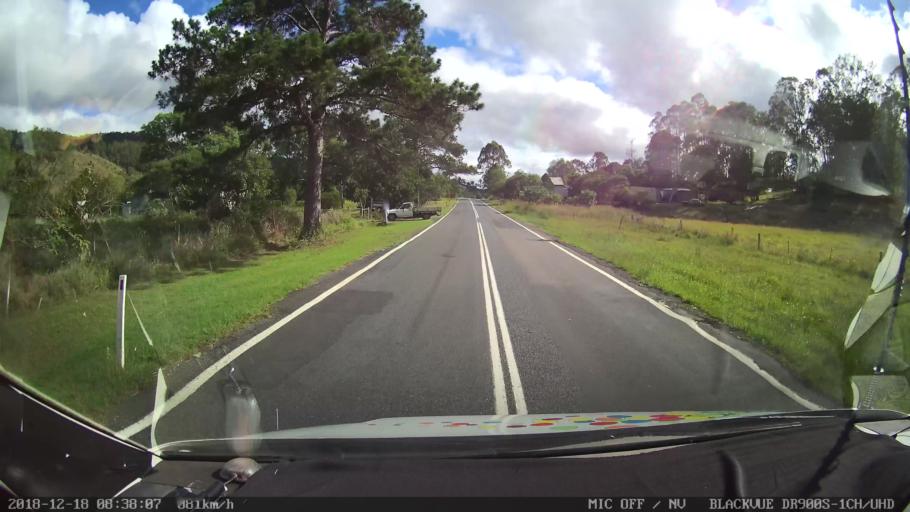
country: AU
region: New South Wales
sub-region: Kyogle
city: Kyogle
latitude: -28.2586
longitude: 152.8245
